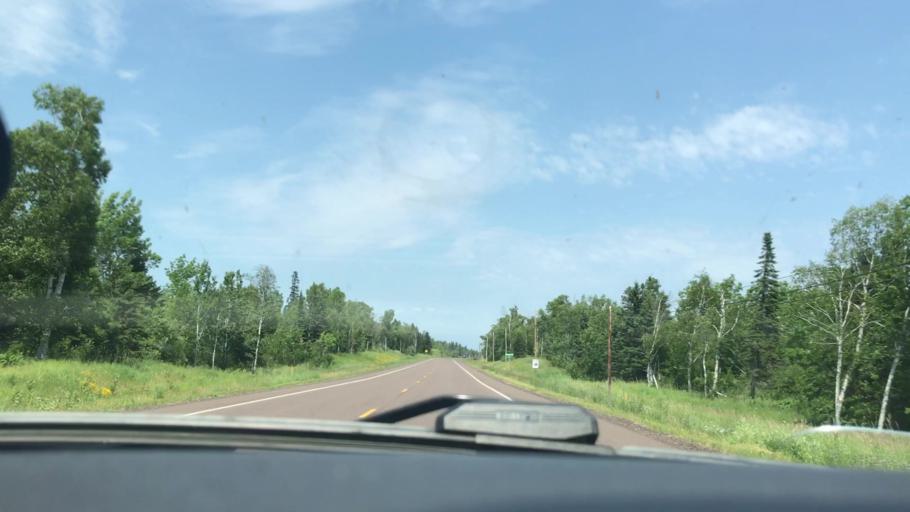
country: US
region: Minnesota
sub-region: Lake County
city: Silver Bay
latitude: 47.4265
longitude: -91.0909
